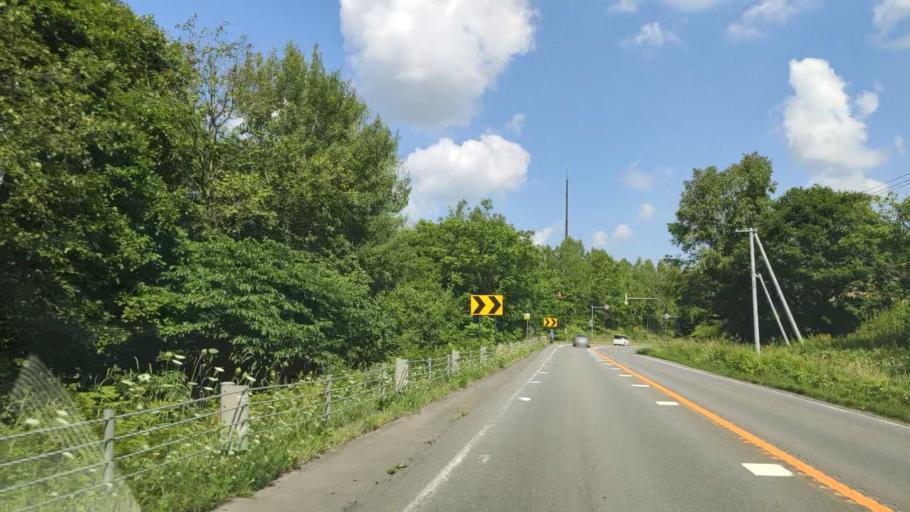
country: JP
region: Hokkaido
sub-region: Asahikawa-shi
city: Asahikawa
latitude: 43.5817
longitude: 142.4374
